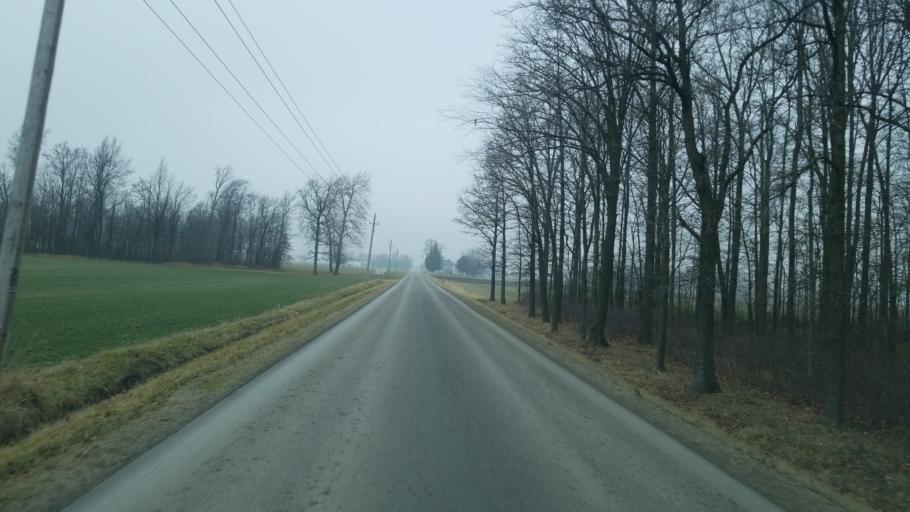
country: US
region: Indiana
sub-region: Adams County
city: Berne
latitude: 40.6763
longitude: -84.9943
